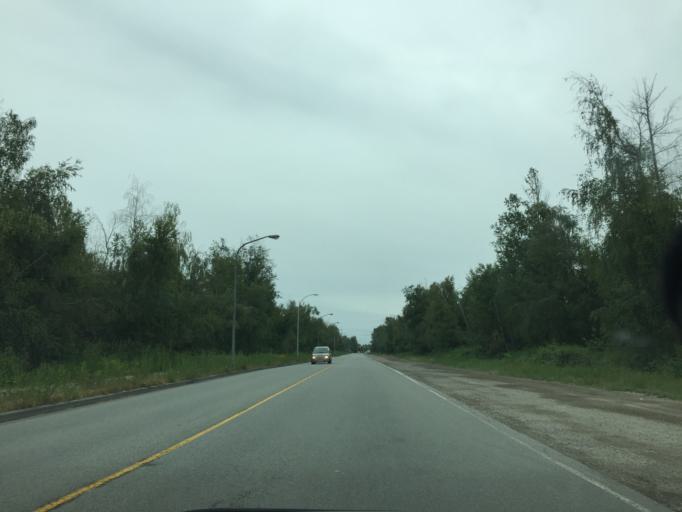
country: CA
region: British Columbia
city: Richmond
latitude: 49.1753
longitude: -123.1031
